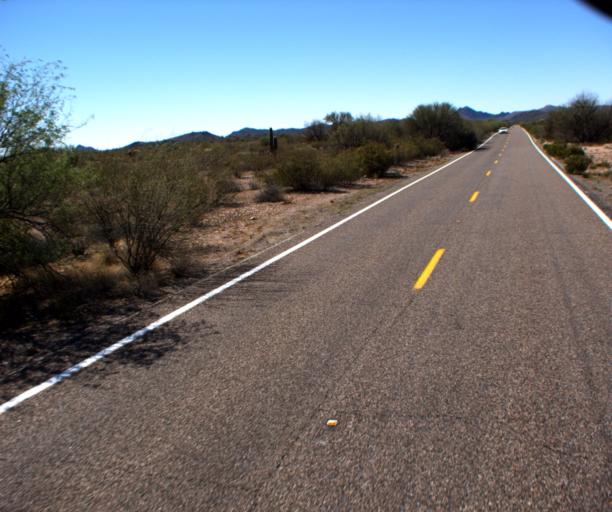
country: MX
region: Sonora
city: Sonoyta
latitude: 32.0399
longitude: -112.7956
